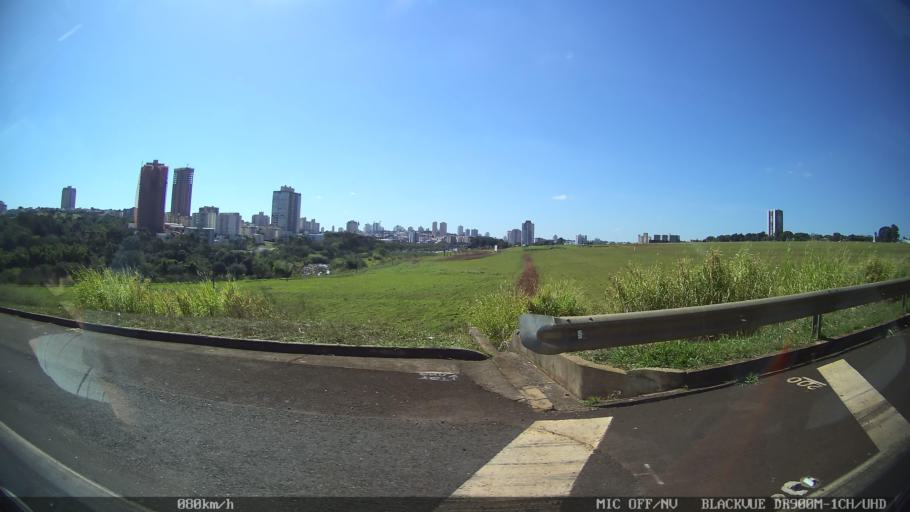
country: BR
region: Sao Paulo
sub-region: Franca
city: Franca
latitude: -20.5591
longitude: -47.4158
